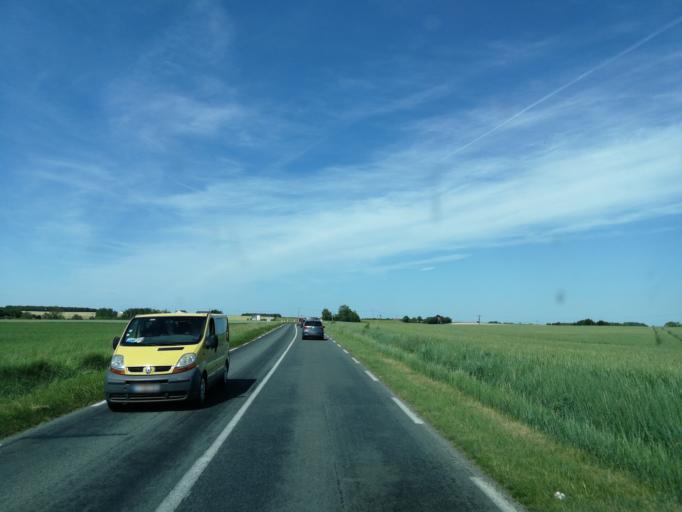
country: FR
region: Poitou-Charentes
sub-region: Departement de la Vienne
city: Loudun
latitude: 47.0210
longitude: 0.1030
